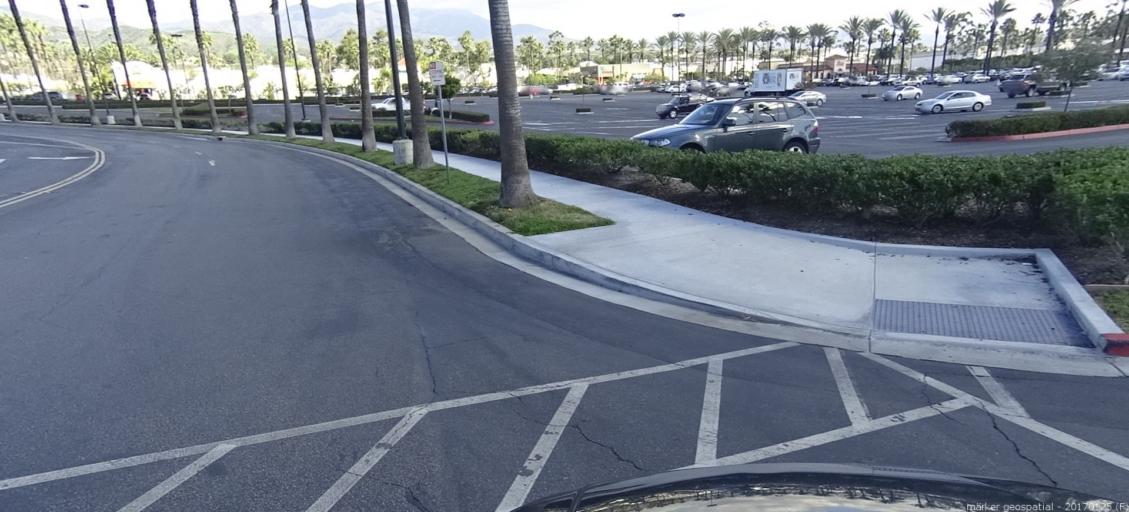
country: US
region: California
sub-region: Orange County
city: Foothill Ranch
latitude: 33.6779
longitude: -117.6693
